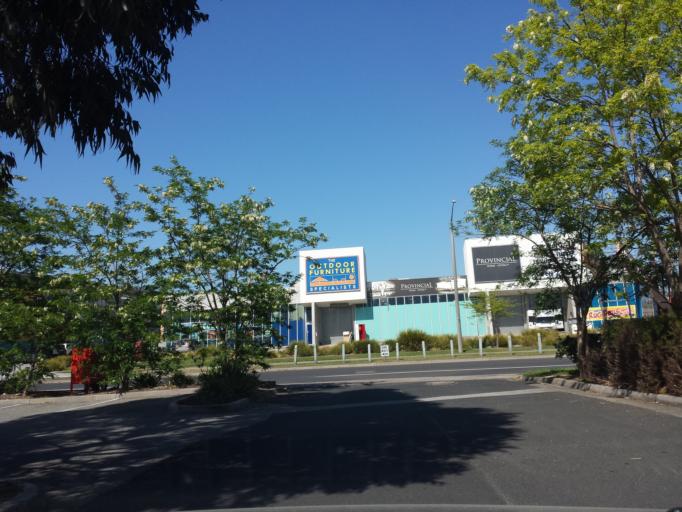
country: AU
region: Victoria
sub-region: Casey
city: Narre Warren
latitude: -38.0233
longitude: 145.3085
